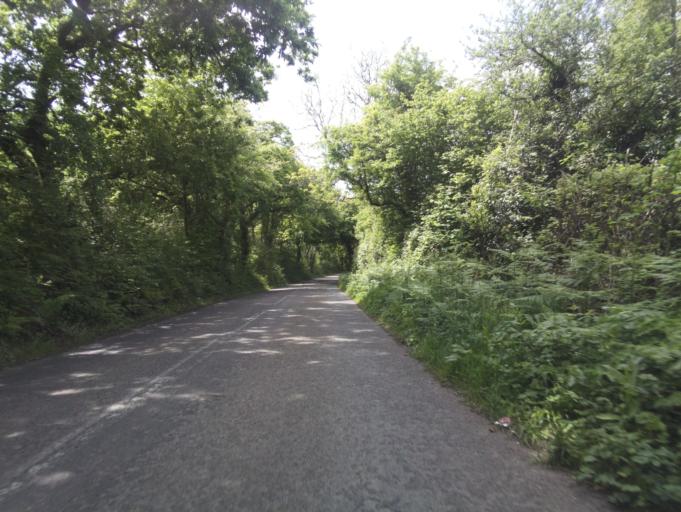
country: GB
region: England
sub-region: Devon
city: Kingsbridge
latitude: 50.3616
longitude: -3.7648
